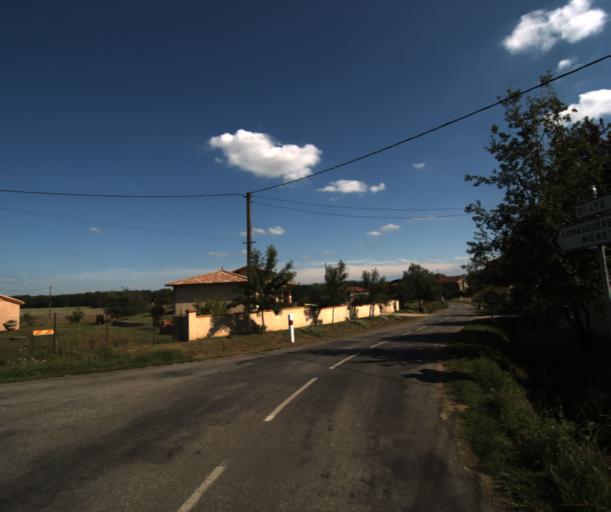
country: FR
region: Midi-Pyrenees
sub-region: Departement de la Haute-Garonne
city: Fonsorbes
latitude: 43.5003
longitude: 1.2196
